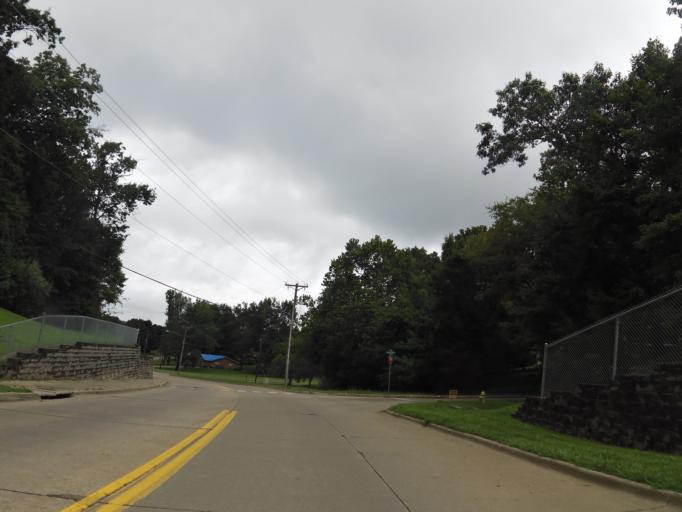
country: US
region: Missouri
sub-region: Cape Girardeau County
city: Cape Girardeau
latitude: 37.3483
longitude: -89.5591
